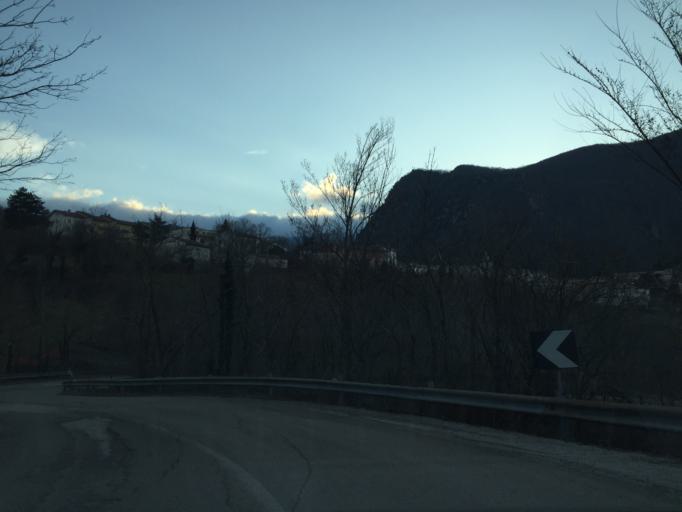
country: IT
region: Molise
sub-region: Provincia di Campobasso
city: Guardiaregia
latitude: 41.4353
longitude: 14.5460
